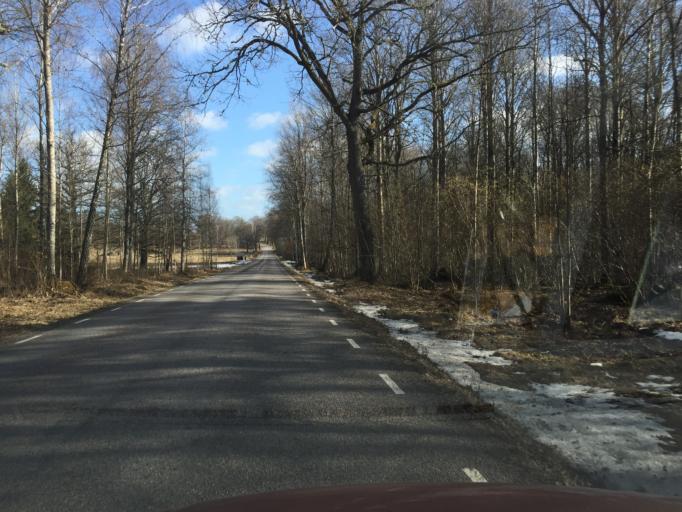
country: SE
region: Soedermanland
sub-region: Vingakers Kommun
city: Vingaker
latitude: 59.0359
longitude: 15.7065
